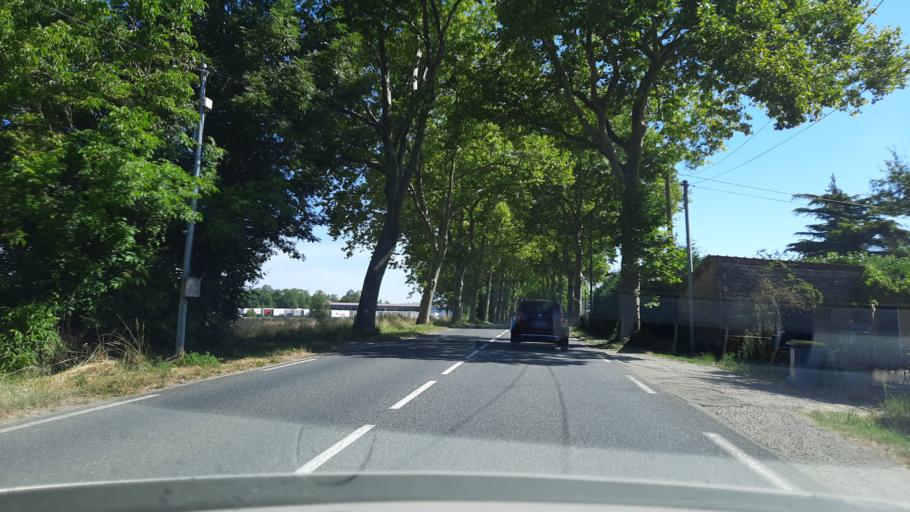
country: FR
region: Midi-Pyrenees
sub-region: Departement du Tarn-et-Garonne
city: Caylus
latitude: 44.3151
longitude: 1.8899
